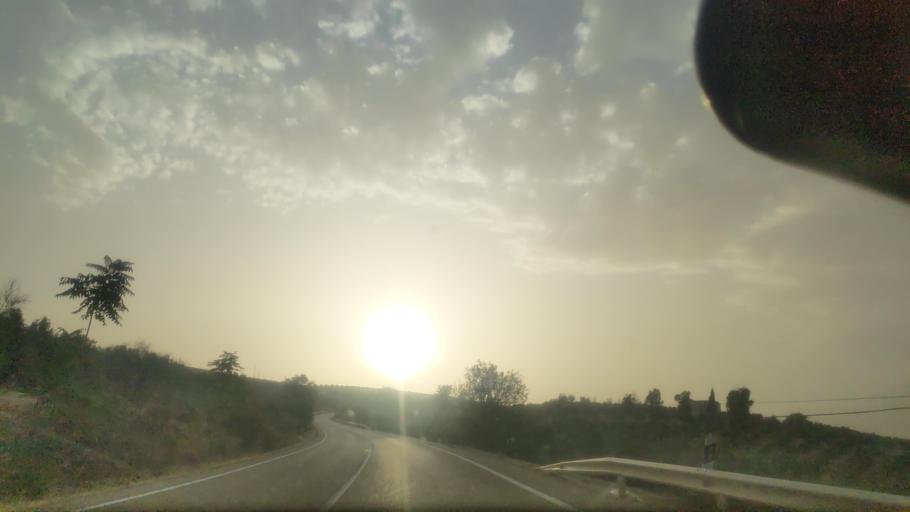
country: ES
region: Andalusia
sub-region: Provincia de Jaen
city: Jimena
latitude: 37.8457
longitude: -3.4949
